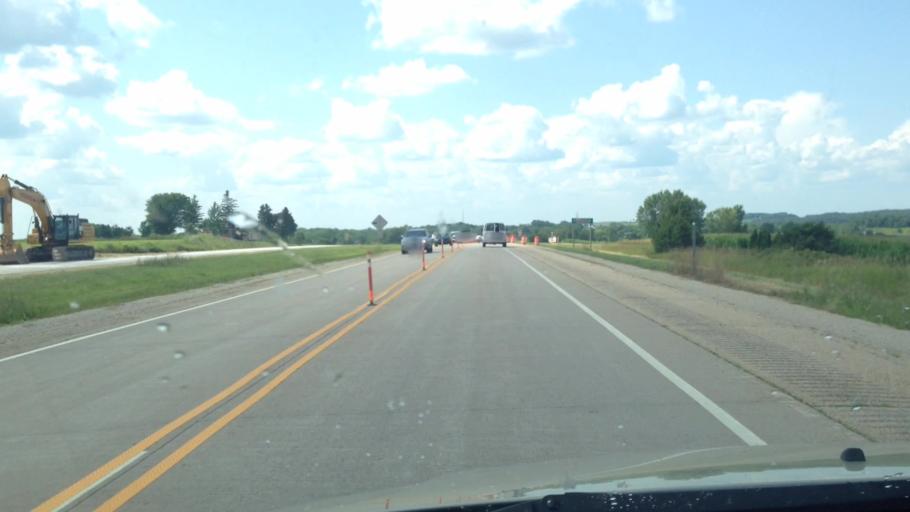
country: US
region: Wisconsin
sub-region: Shawano County
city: Bonduel
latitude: 44.7000
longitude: -88.3603
